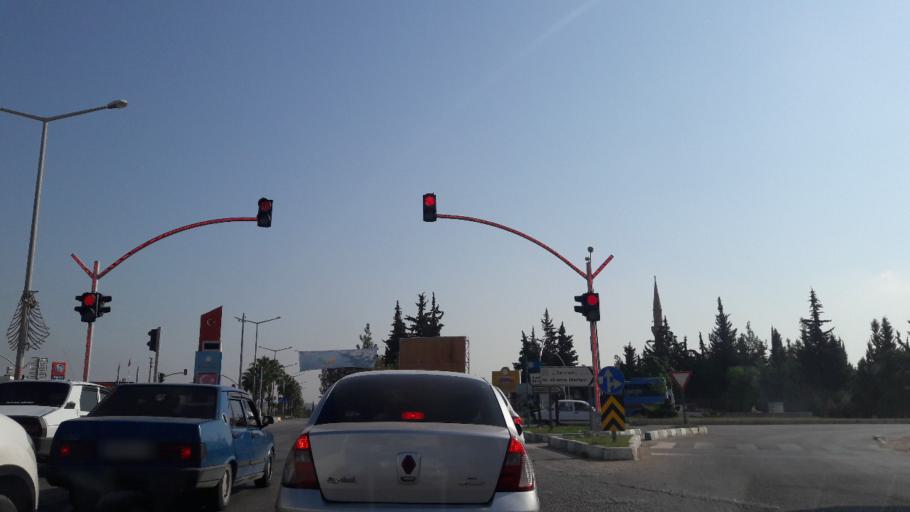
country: TR
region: Adana
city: Yuregir
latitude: 37.0415
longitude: 35.4296
